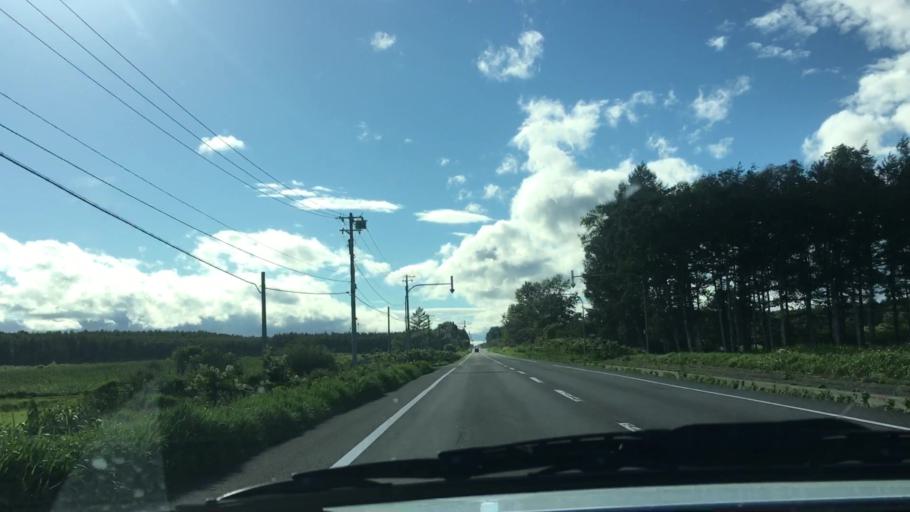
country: JP
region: Hokkaido
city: Otofuke
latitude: 43.1616
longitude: 143.1579
